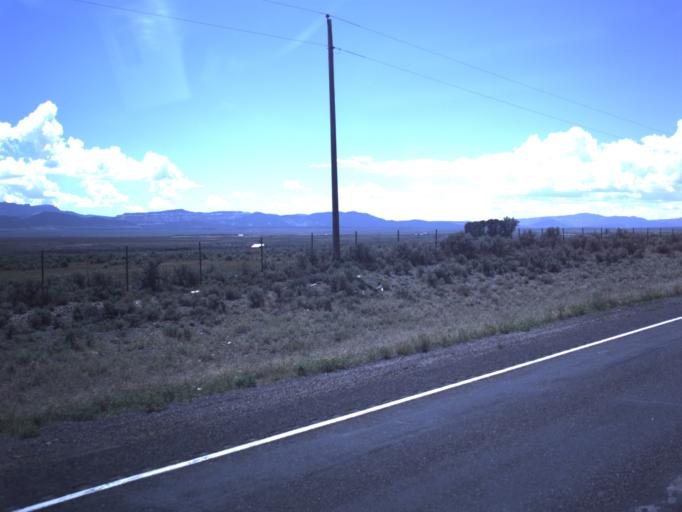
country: US
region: Utah
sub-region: Garfield County
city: Panguitch
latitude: 37.9228
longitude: -112.4272
